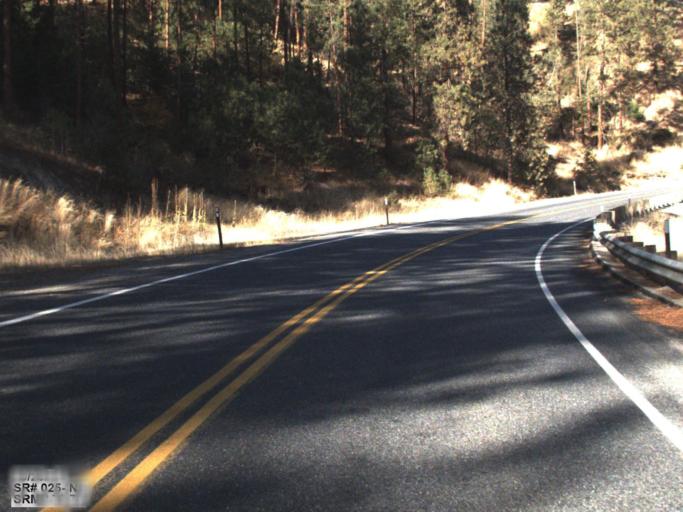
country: US
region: Washington
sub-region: Stevens County
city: Kettle Falls
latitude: 48.5766
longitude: -118.0839
